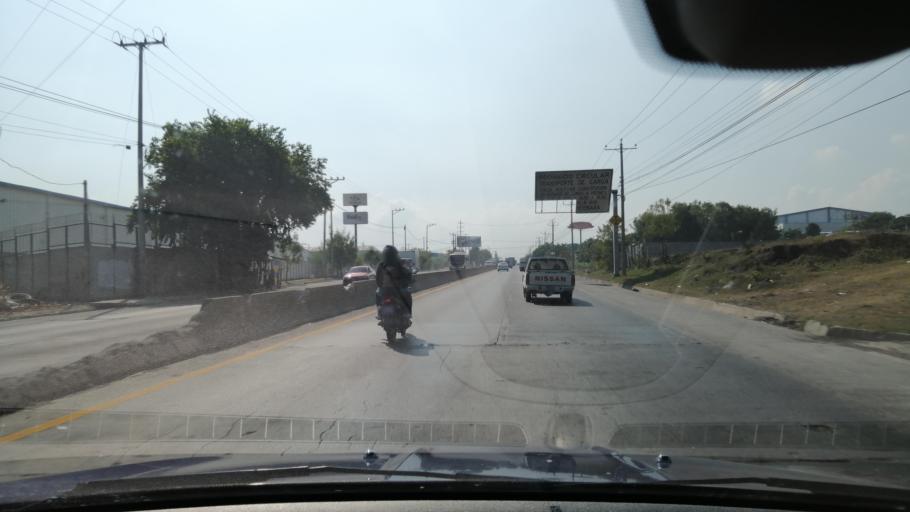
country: SV
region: La Libertad
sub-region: Distrito de Quezaltepeque
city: Quezaltepeque
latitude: 13.8031
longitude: -89.2353
